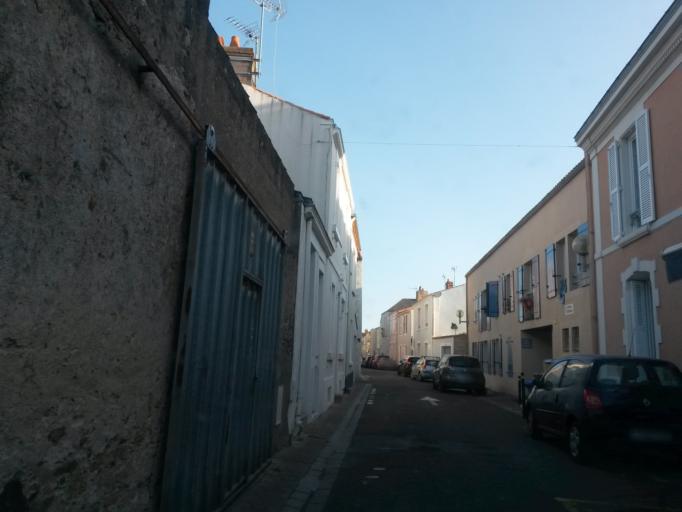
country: FR
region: Pays de la Loire
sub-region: Departement de la Vendee
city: Les Sables-d'Olonne
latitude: 46.4967
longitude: -1.7977
